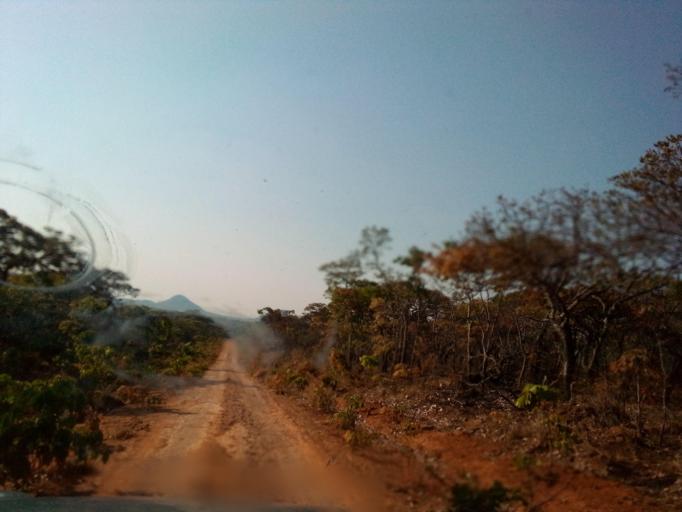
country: ZM
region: Northern
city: Mpika
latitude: -12.2162
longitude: 31.4394
